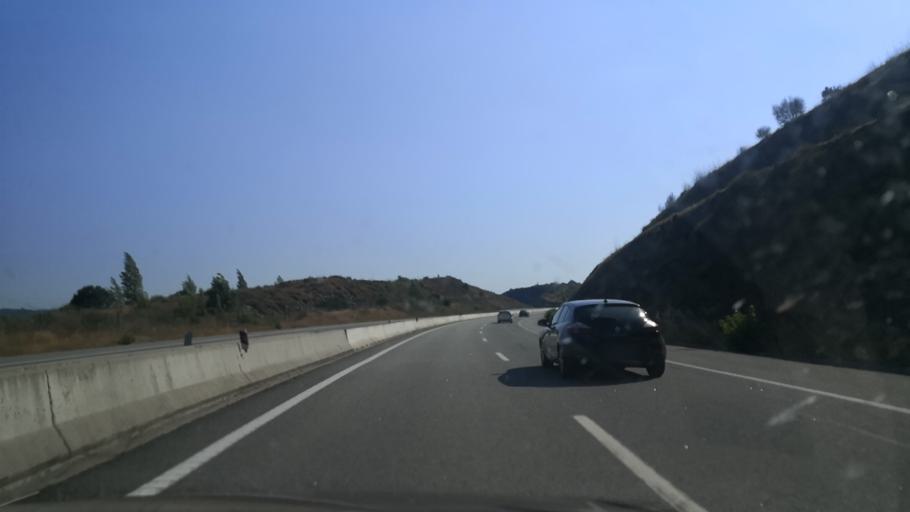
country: PT
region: Braganca
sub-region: Mirandela
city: Mirandela
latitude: 41.5259
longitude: -7.0968
